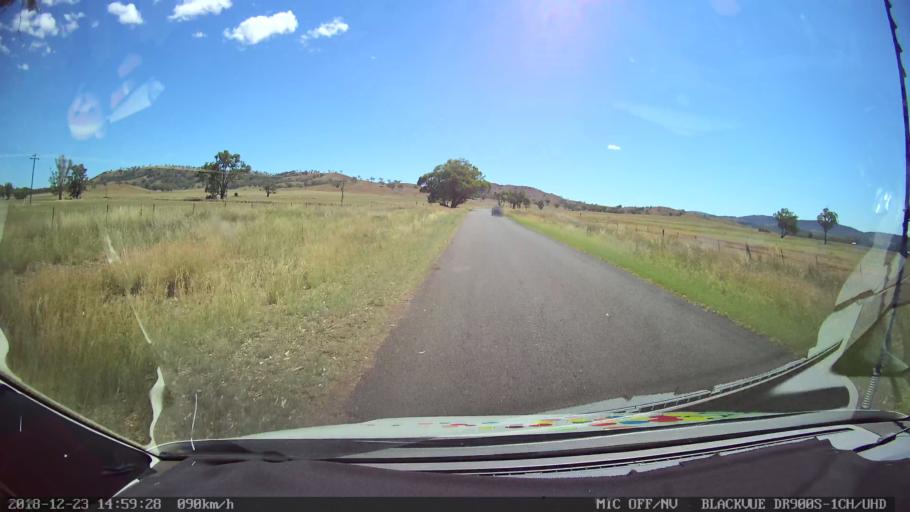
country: AU
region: New South Wales
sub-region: Tamworth Municipality
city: Manilla
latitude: -30.7241
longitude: 150.8001
